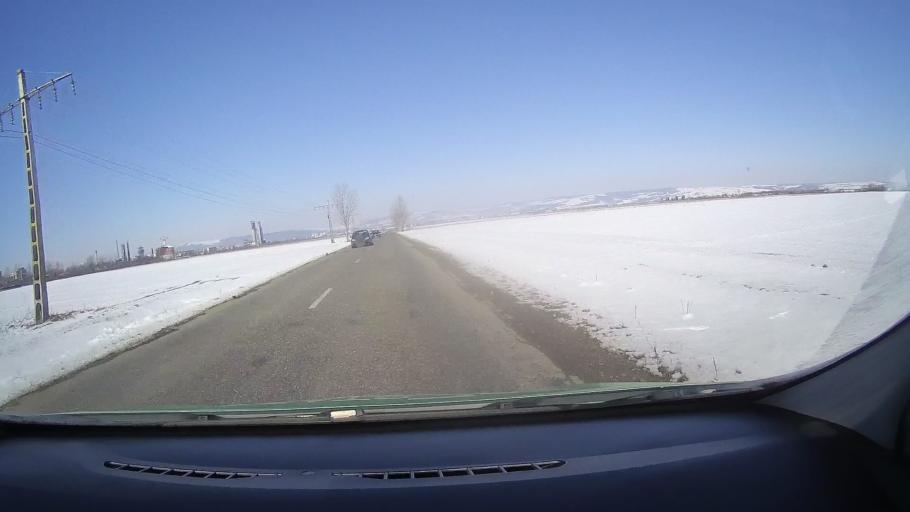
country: RO
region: Brasov
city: Fogarasch
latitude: 45.8009
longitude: 24.9929
